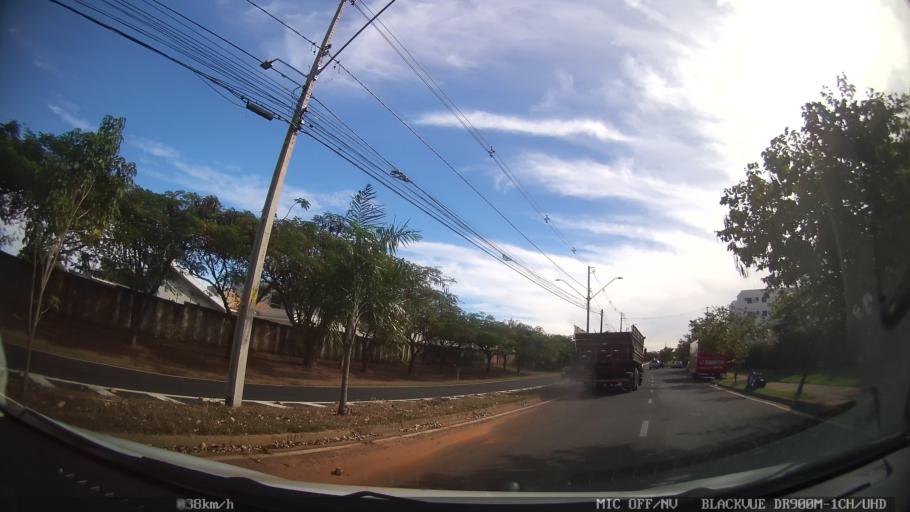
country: BR
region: Sao Paulo
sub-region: Catanduva
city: Catanduva
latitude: -21.1209
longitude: -48.9779
